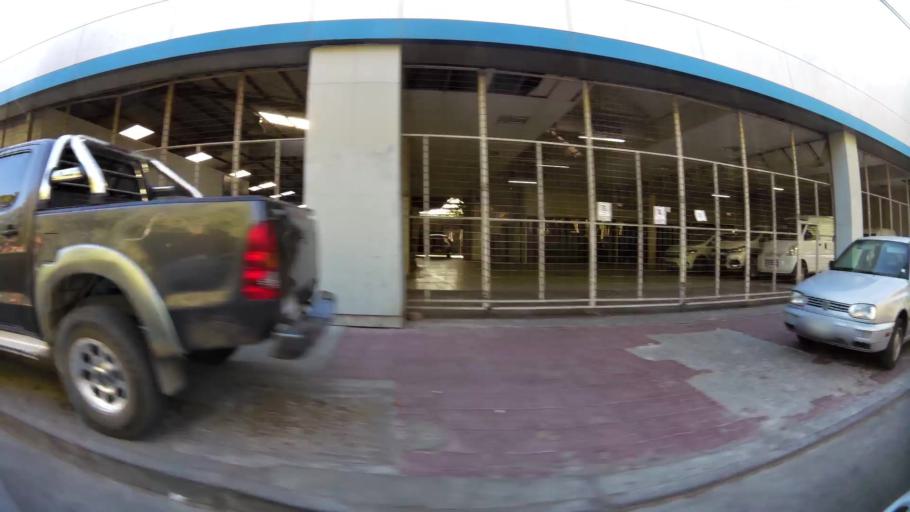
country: CL
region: Maule
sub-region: Provincia de Curico
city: Curico
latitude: -34.9825
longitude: -71.2348
